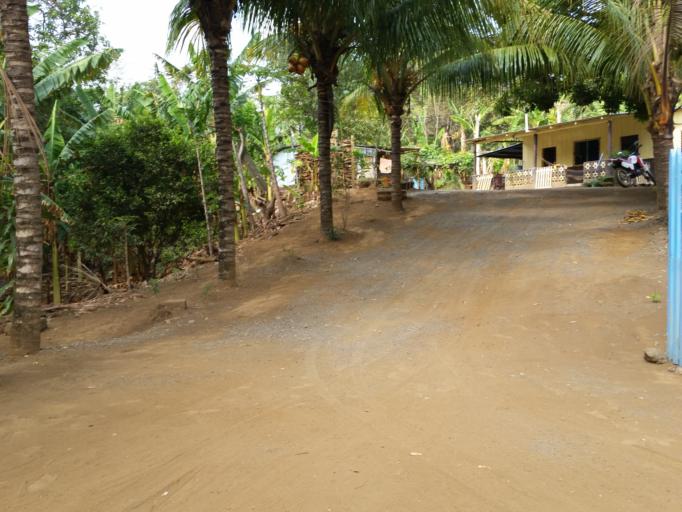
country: NI
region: Masaya
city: Ticuantepe
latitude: 12.0620
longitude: -86.2503
